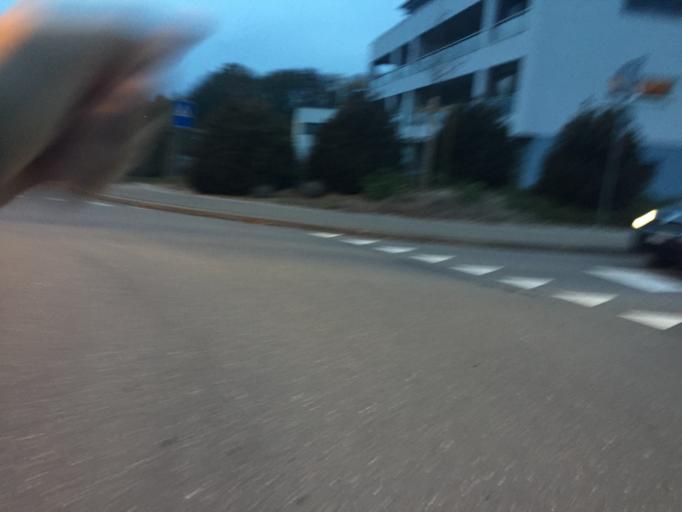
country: CH
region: Fribourg
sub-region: See District
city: Murten
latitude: 46.9386
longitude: 7.1331
